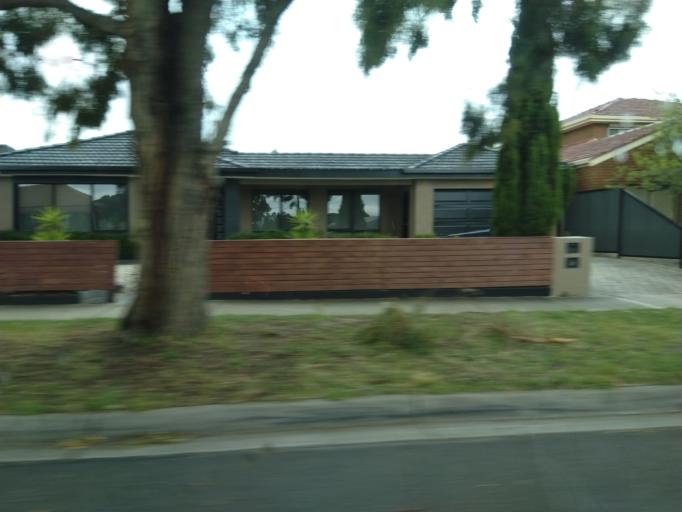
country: AU
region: Victoria
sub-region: Hume
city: Meadow Heights
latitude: -37.6468
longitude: 144.8980
